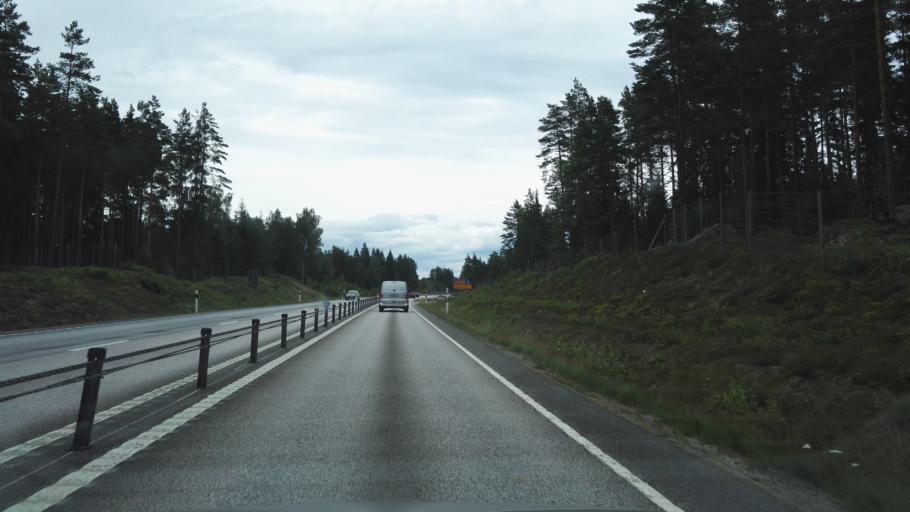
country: SE
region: Kronoberg
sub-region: Vaxjo Kommun
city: Braas
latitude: 56.9952
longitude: 15.0074
